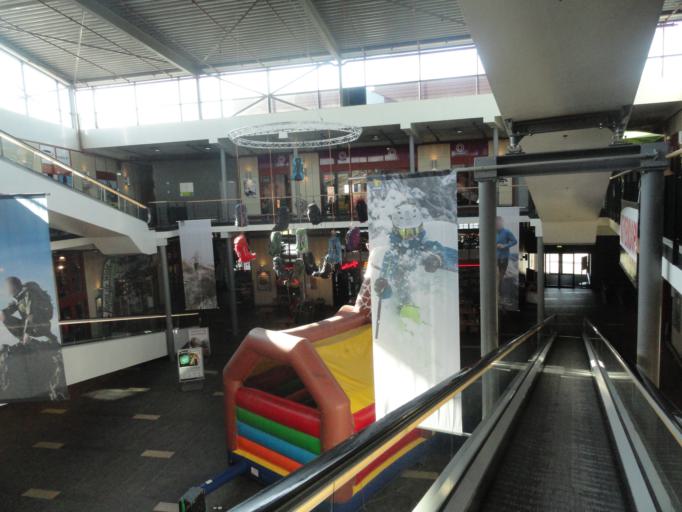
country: NL
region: Utrecht
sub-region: Gemeente Houten
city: Houten
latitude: 52.0242
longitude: 5.1461
